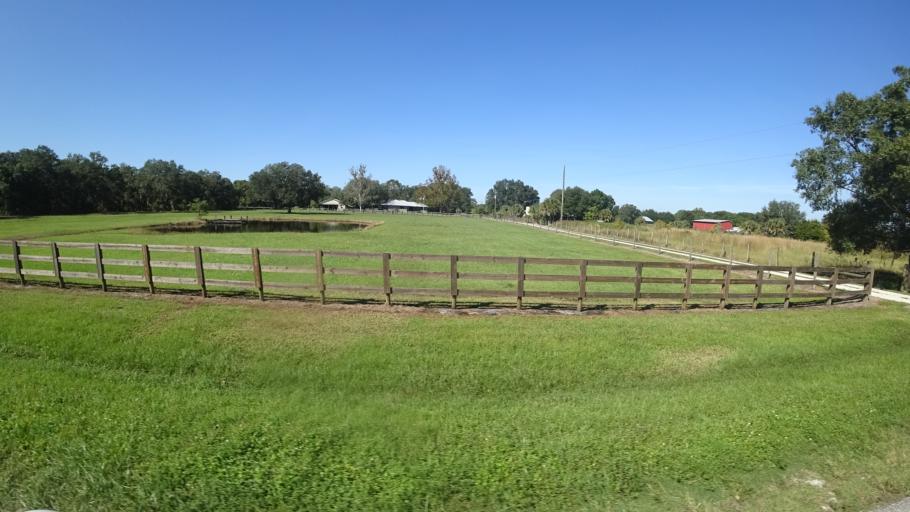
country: US
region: Florida
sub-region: Sarasota County
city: Lake Sarasota
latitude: 27.3103
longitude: -82.2671
